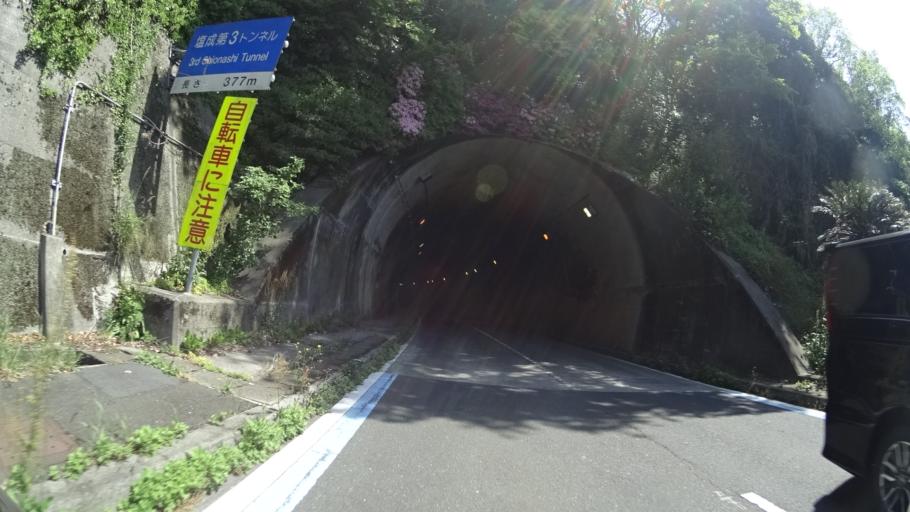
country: JP
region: Ehime
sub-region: Nishiuwa-gun
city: Ikata-cho
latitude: 33.4318
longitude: 132.2282
